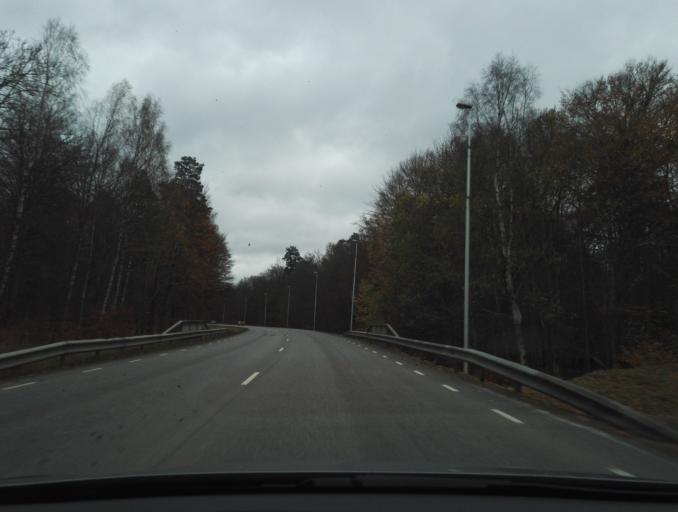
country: SE
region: Kronoberg
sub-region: Vaxjo Kommun
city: Vaexjoe
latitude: 56.8676
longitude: 14.7888
